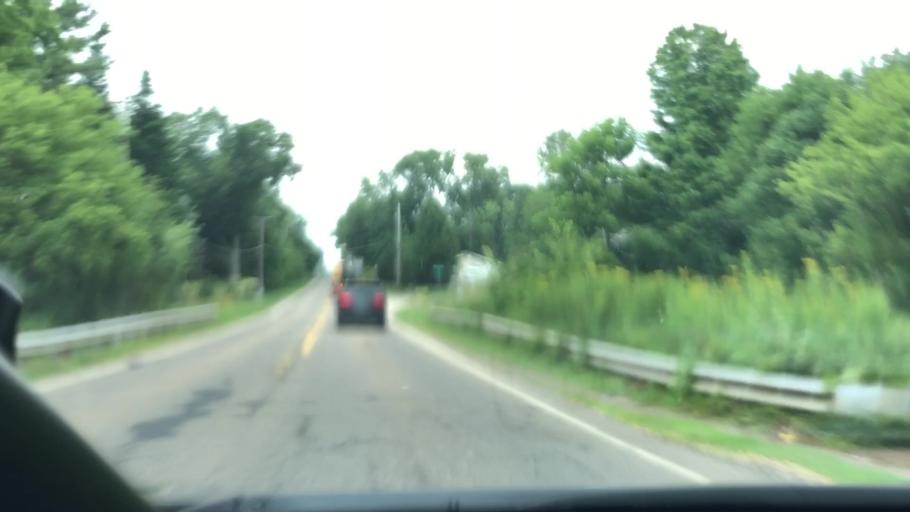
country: US
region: Ohio
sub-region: Summit County
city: New Franklin
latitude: 40.9160
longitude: -81.5361
